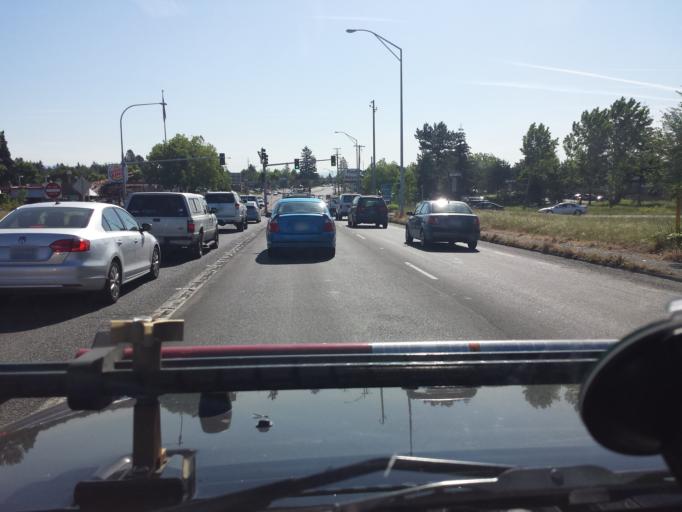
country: US
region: Washington
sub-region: Clark County
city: Orchards
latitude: 45.6210
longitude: -122.5584
